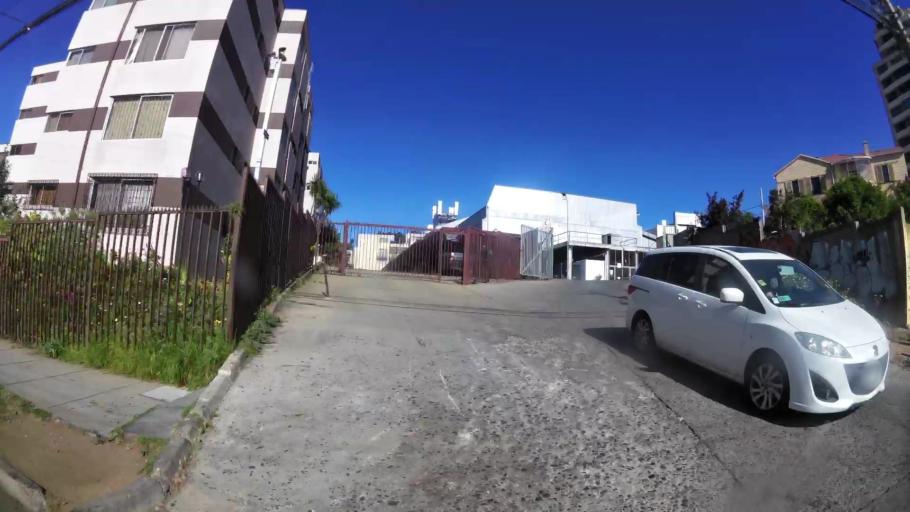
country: CL
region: Valparaiso
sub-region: Provincia de Valparaiso
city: Vina del Mar
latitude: -33.0284
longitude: -71.5579
